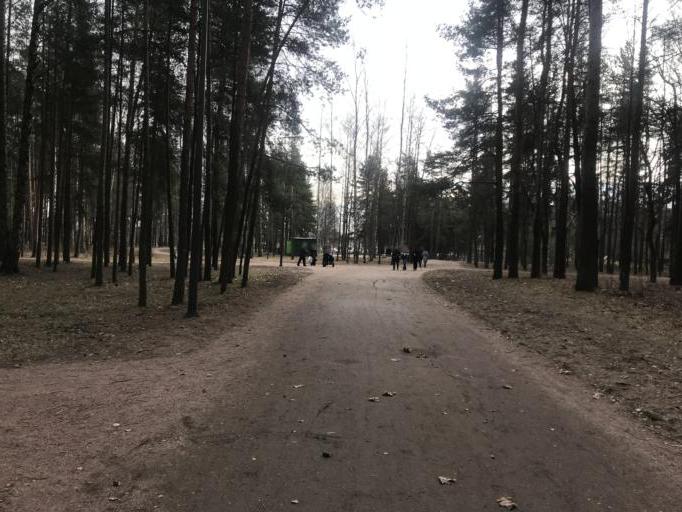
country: RU
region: St.-Petersburg
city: Sosnovka
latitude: 60.0151
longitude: 30.3507
